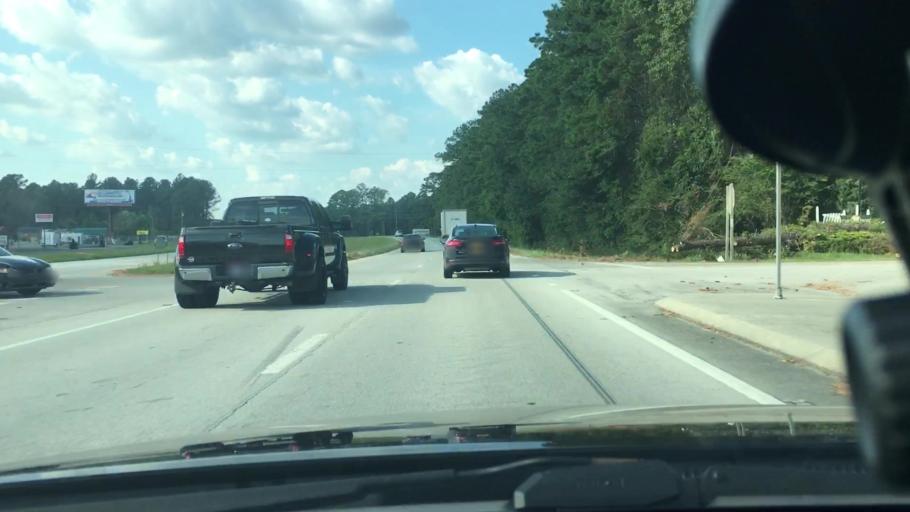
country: US
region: North Carolina
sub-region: Craven County
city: Neuse Forest
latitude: 34.9560
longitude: -76.9499
